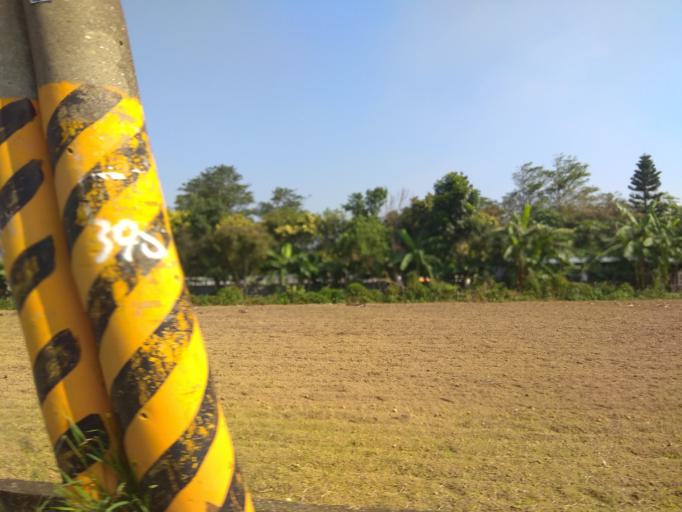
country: TW
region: Taiwan
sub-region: Hsinchu
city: Zhubei
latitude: 24.9831
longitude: 121.0788
